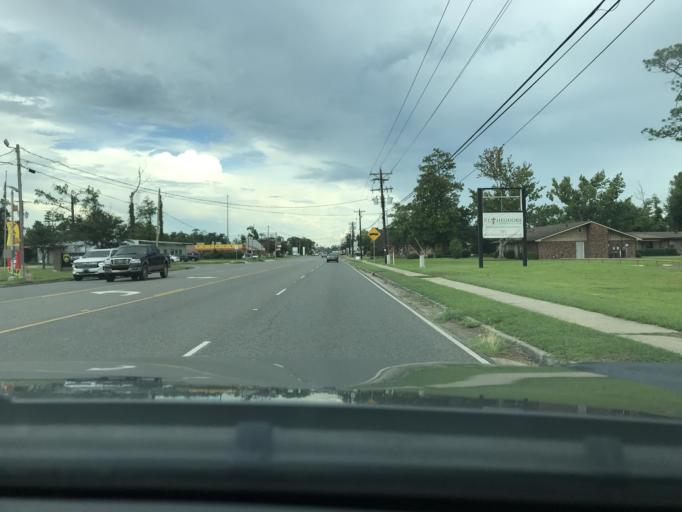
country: US
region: Louisiana
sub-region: Calcasieu Parish
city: Moss Bluff
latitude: 30.3006
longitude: -93.2106
